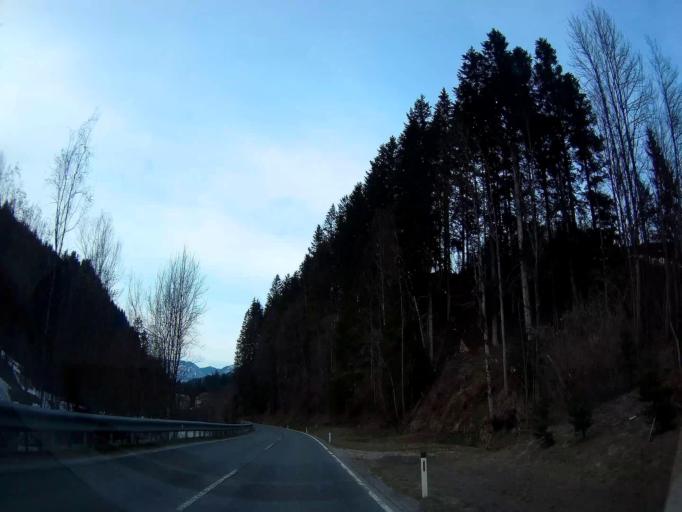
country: AT
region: Salzburg
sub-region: Politischer Bezirk Hallein
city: Abtenau
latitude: 47.5346
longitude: 13.4239
